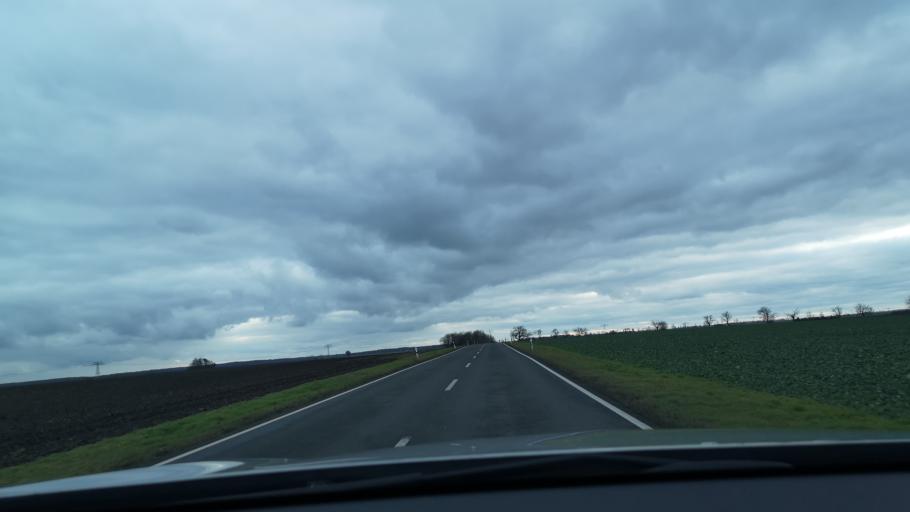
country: DE
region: Saxony-Anhalt
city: Mucheln
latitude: 51.2939
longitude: 11.8001
